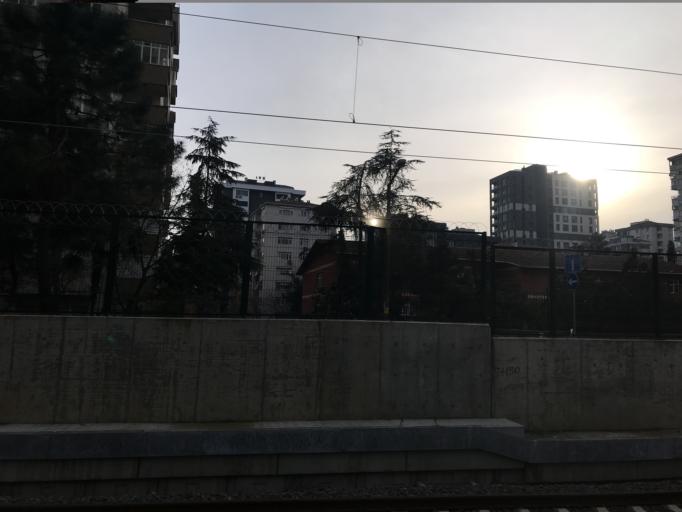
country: TR
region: Istanbul
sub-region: Atasehir
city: Atasehir
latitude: 40.9780
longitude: 29.0686
